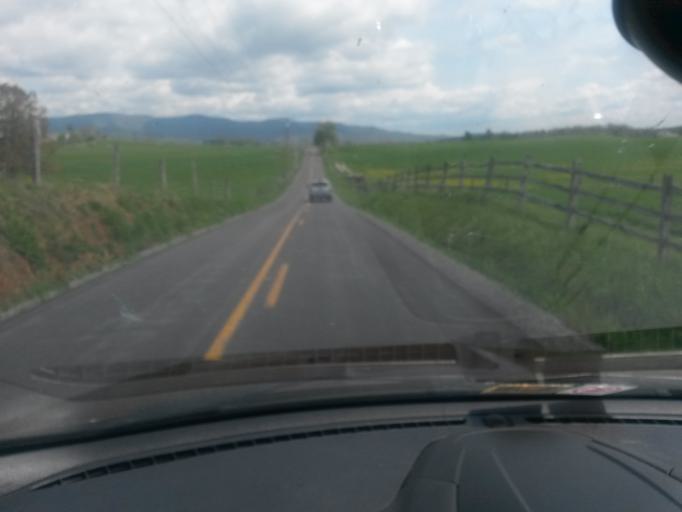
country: US
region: West Virginia
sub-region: Pocahontas County
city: Marlinton
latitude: 38.1131
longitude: -80.2163
